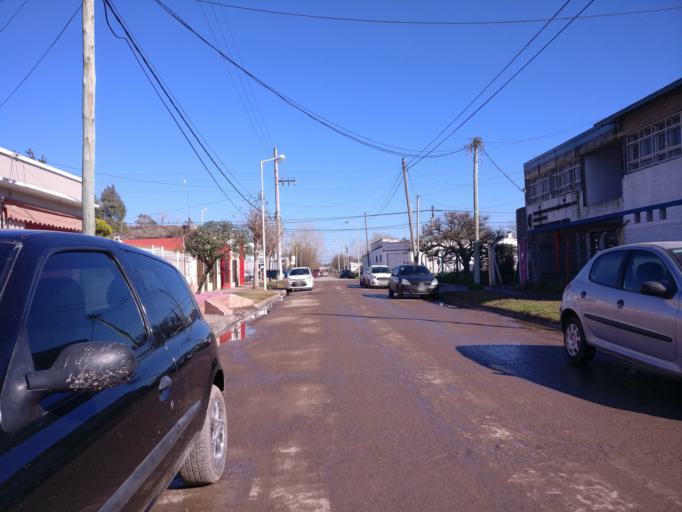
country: AR
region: Buenos Aires
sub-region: Partido de Ezeiza
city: Ezeiza
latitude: -34.9397
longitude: -58.6167
